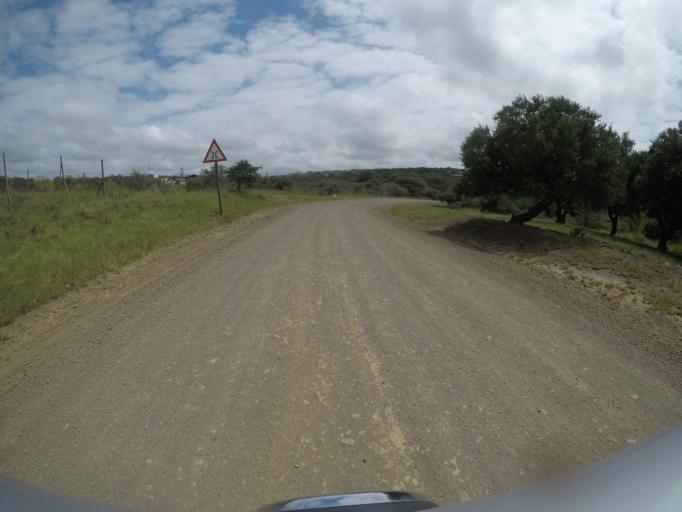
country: ZA
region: KwaZulu-Natal
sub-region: uThungulu District Municipality
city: Empangeni
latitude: -28.6119
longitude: 31.8447
